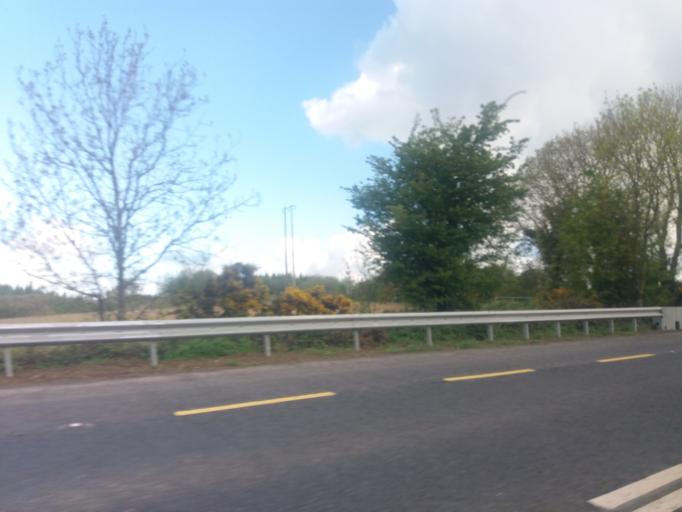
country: IE
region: Leinster
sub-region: Loch Garman
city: Ferns
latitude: 52.5805
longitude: -6.5146
